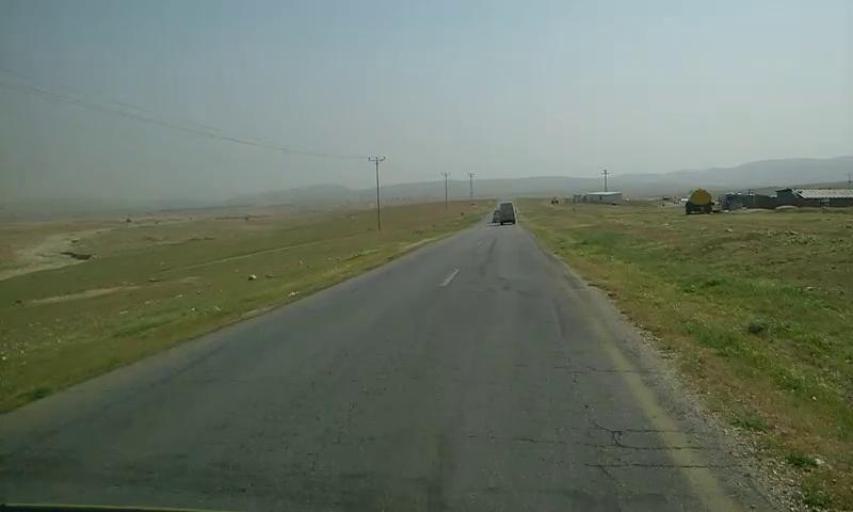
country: PS
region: West Bank
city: An Nuway`imah
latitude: 31.9200
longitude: 35.3987
